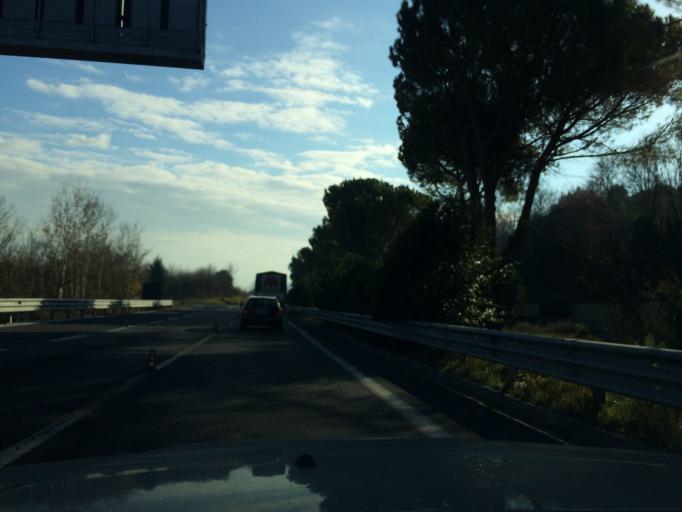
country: IT
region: Umbria
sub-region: Provincia di Terni
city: San Gemini
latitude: 42.6212
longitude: 12.5525
